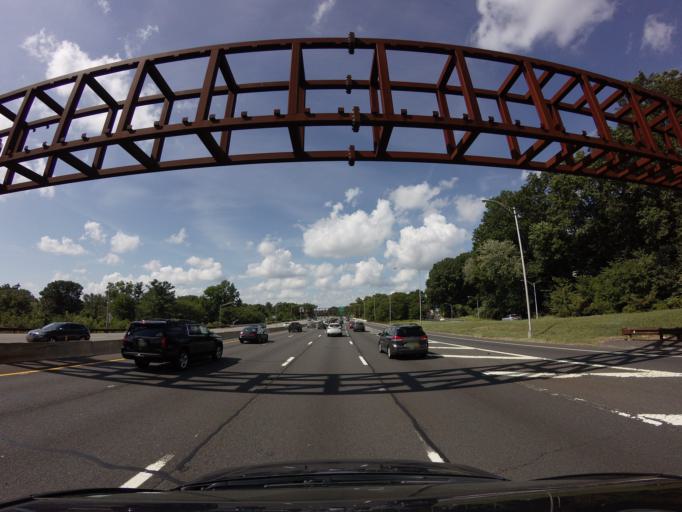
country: US
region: New Jersey
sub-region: Union County
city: Union
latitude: 40.6926
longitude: -74.2650
